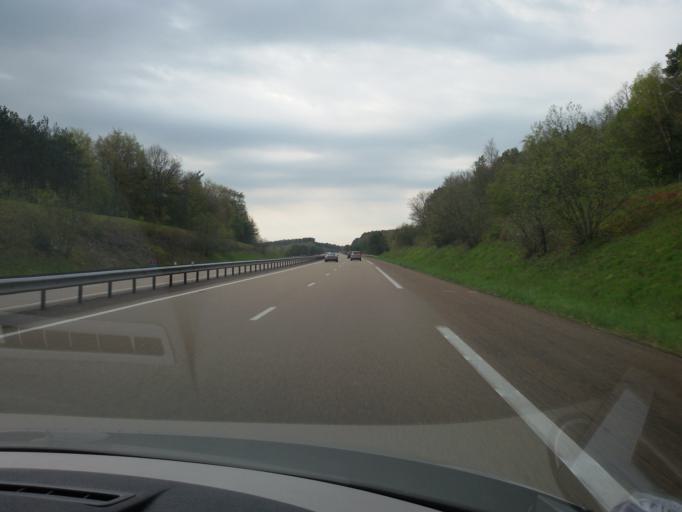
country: FR
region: Champagne-Ardenne
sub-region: Departement de la Haute-Marne
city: Chamarandes-Choignes
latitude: 48.0002
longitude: 5.1173
